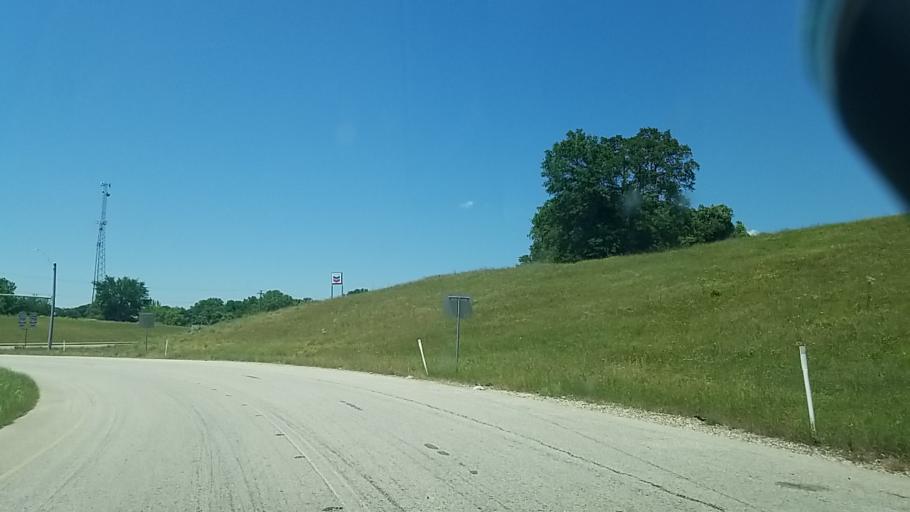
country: US
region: Texas
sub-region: Leon County
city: Buffalo
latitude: 31.4514
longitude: -96.0748
